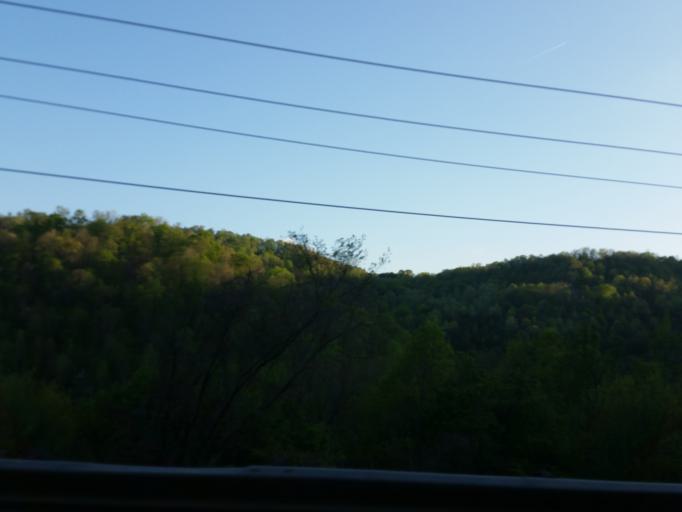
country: US
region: Tennessee
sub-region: Campbell County
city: Jellico
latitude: 36.5384
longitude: -84.0105
